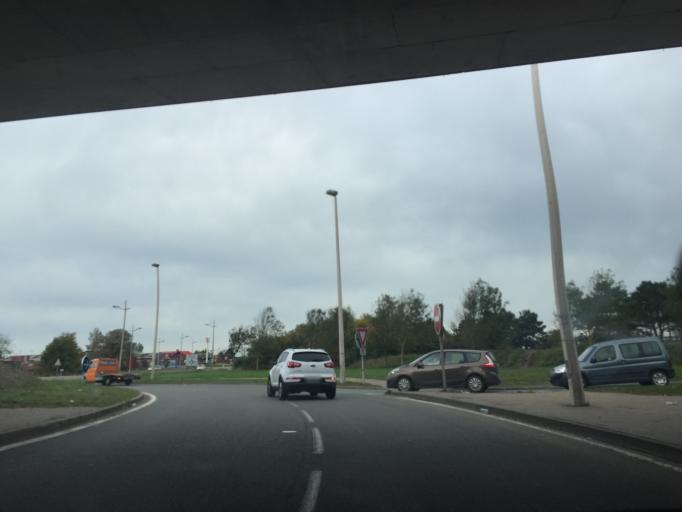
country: FR
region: Nord-Pas-de-Calais
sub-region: Departement du Pas-de-Calais
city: Calais
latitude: 50.9388
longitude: 1.8379
